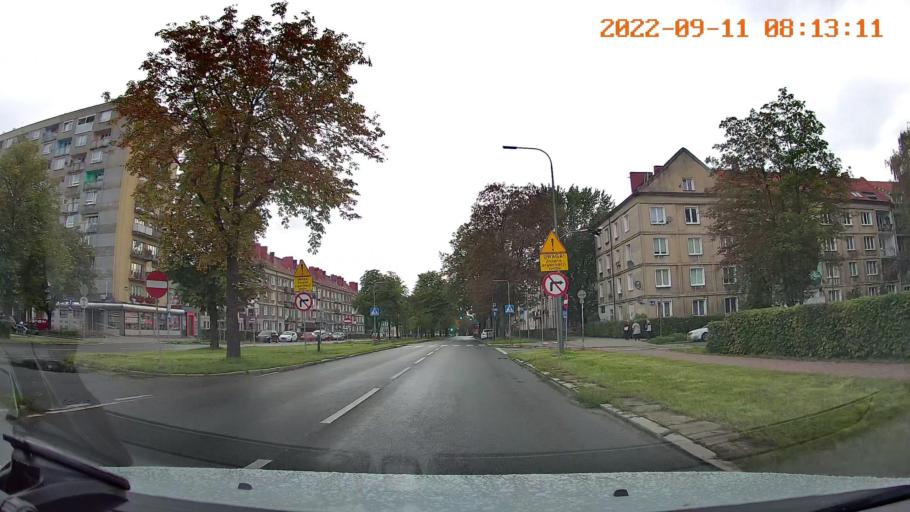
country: PL
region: Silesian Voivodeship
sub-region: Tychy
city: Tychy
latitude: 50.1179
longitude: 18.9832
